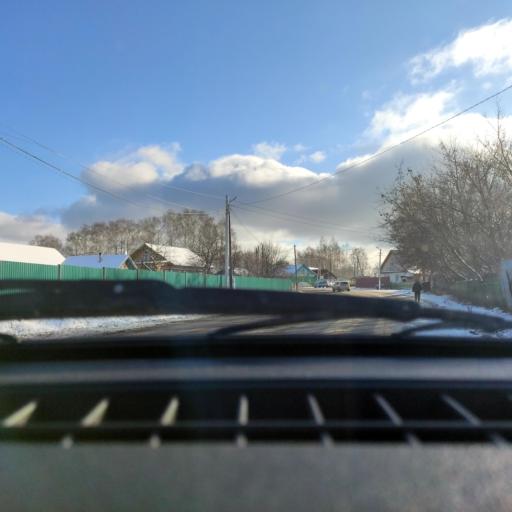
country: RU
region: Bashkortostan
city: Iglino
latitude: 54.8212
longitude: 56.3976
